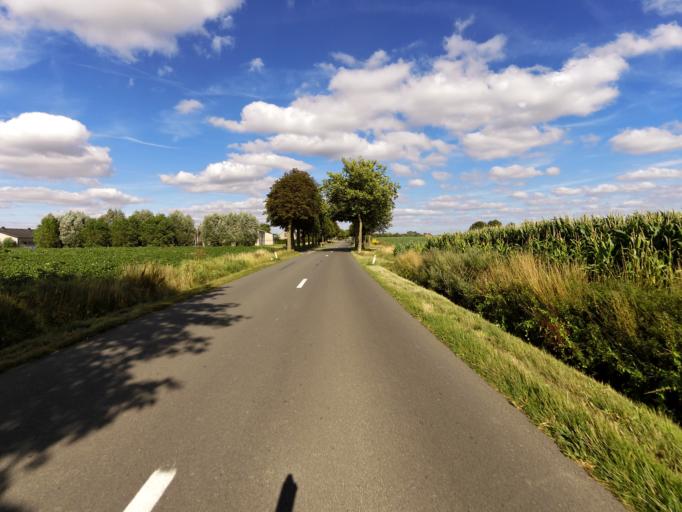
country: BE
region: Flanders
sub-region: Provincie West-Vlaanderen
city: Alveringem
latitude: 50.9724
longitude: 2.6850
